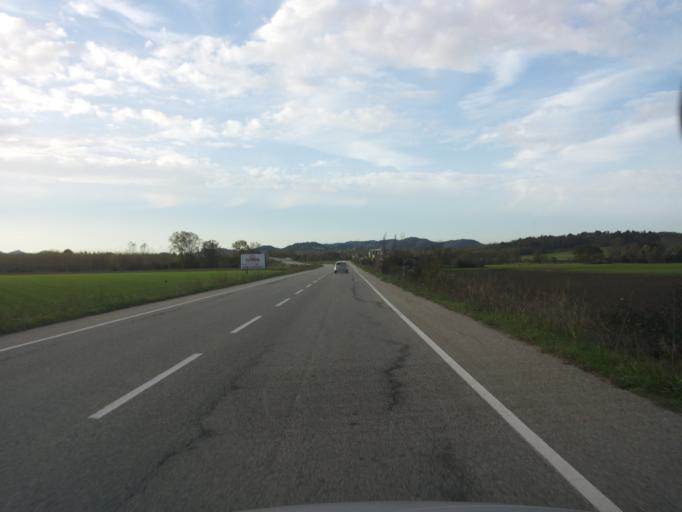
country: IT
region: Piedmont
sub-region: Provincia di Alessandria
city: Cereseto
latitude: 45.1111
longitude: 8.3286
